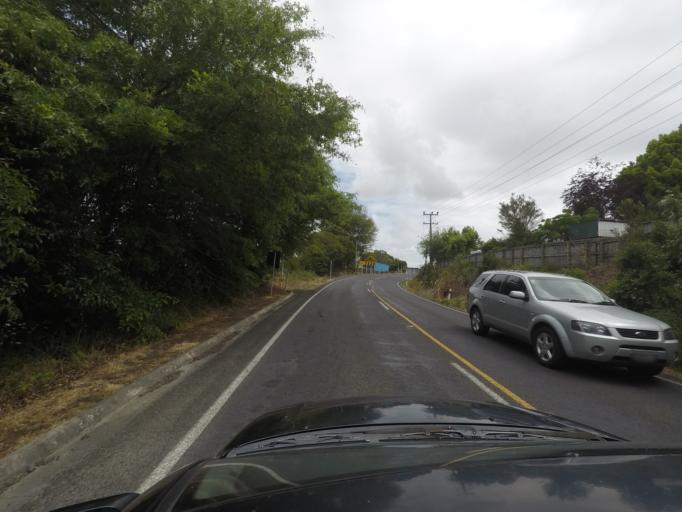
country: NZ
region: Auckland
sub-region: Auckland
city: Parakai
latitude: -36.6255
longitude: 174.5021
